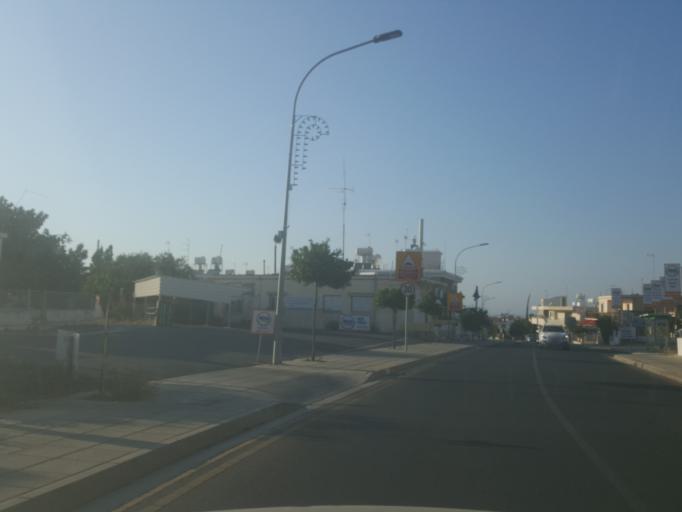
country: CY
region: Ammochostos
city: Deryneia
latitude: 35.0662
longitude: 33.9609
